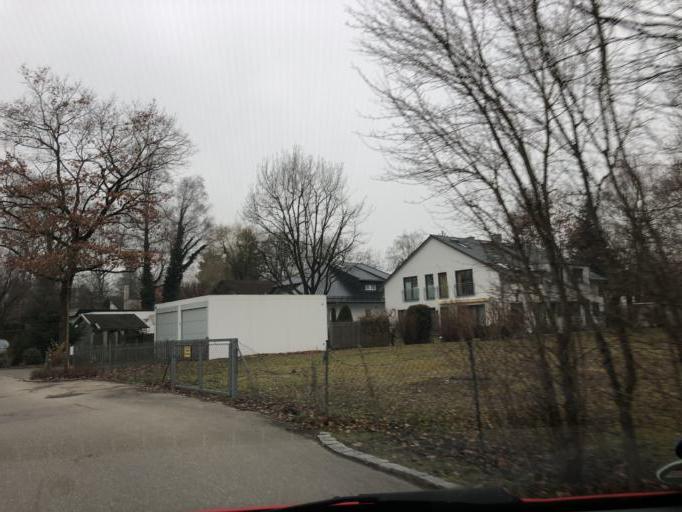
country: DE
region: Bavaria
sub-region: Upper Bavaria
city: Grobenzell
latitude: 48.2034
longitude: 11.3745
